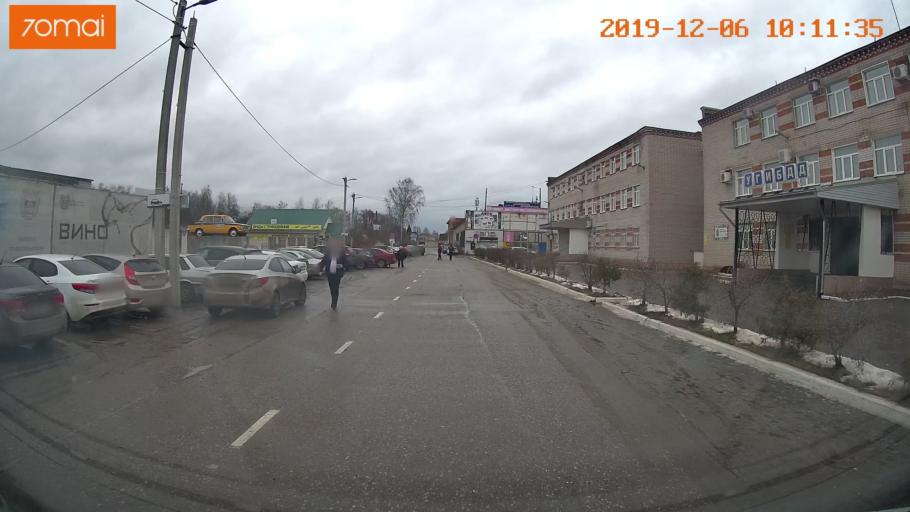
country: RU
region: Ivanovo
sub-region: Gorod Ivanovo
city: Ivanovo
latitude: 57.0312
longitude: 40.9748
